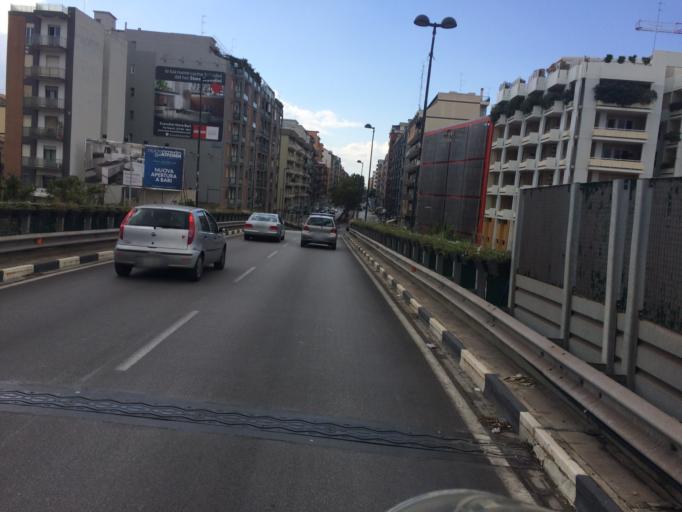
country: IT
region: Apulia
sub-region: Provincia di Bari
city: Bari
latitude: 41.1179
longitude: 16.8729
